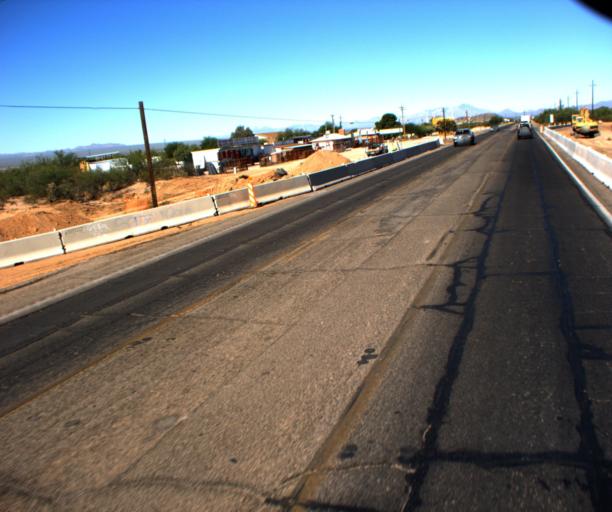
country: US
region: Arizona
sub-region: Pima County
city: Tucson Estates
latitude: 32.1677
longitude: -111.0845
